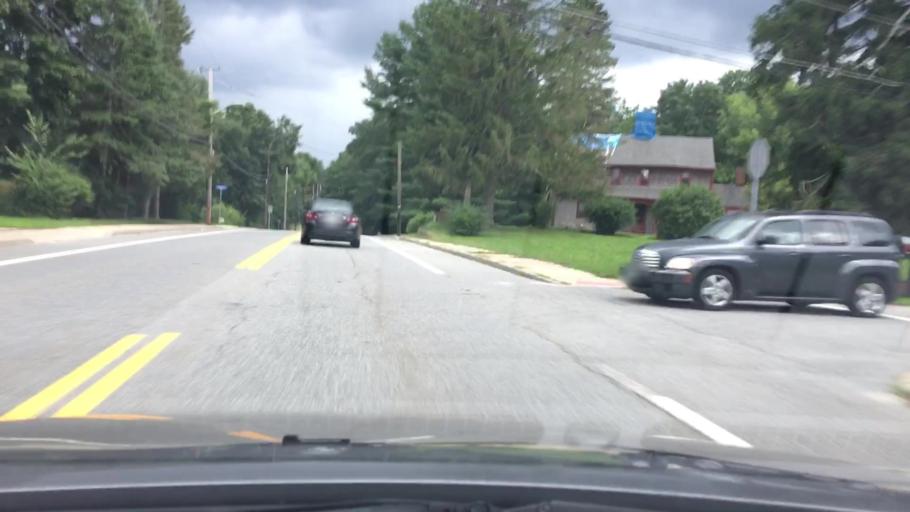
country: US
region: Rhode Island
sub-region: Providence County
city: Cumberland
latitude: 41.9758
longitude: -71.3890
